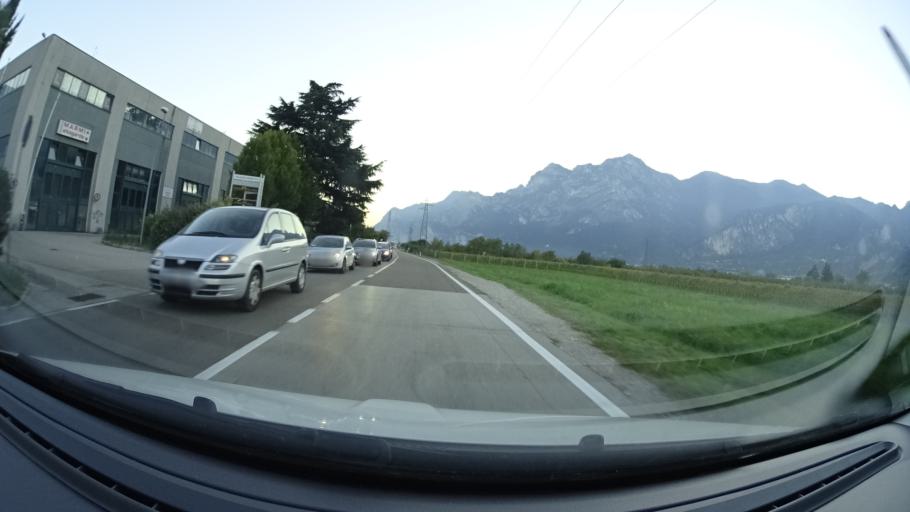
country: IT
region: Trentino-Alto Adige
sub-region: Provincia di Trento
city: Arco
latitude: 45.9071
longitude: 10.8767
